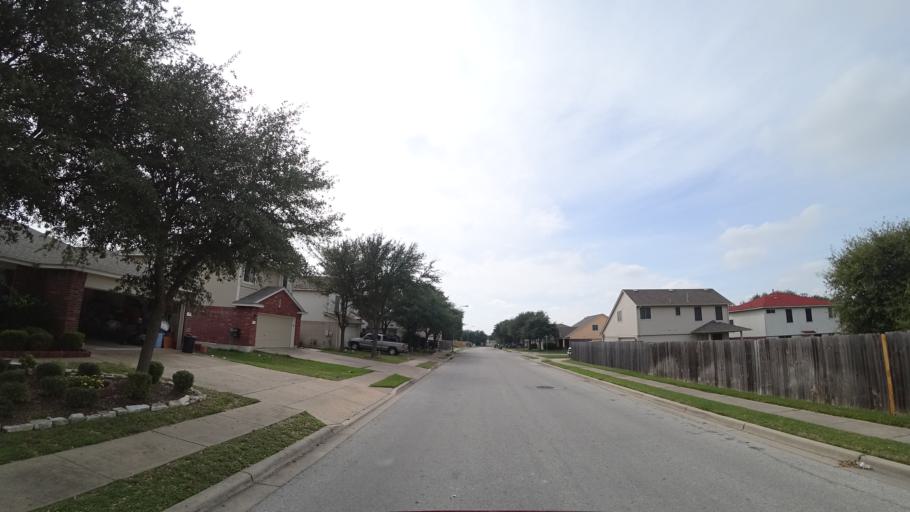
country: US
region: Texas
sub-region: Travis County
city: Windemere
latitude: 30.4451
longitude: -97.6547
